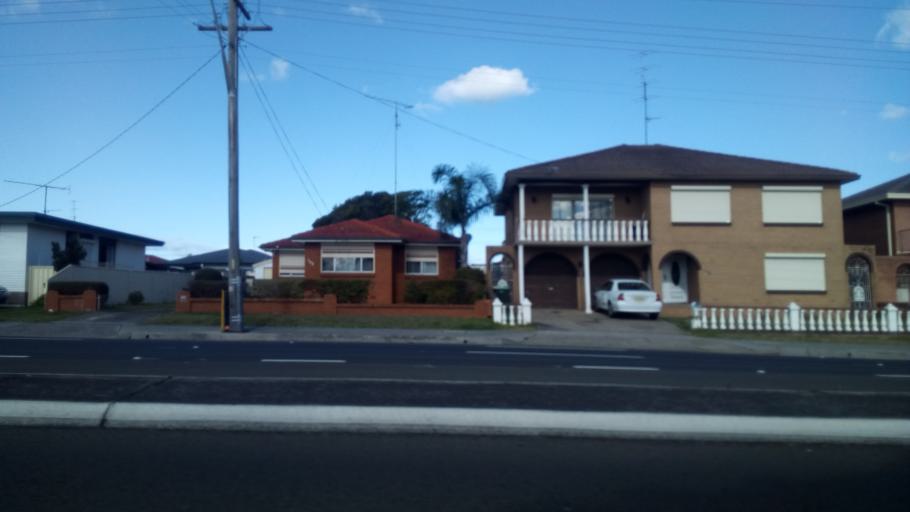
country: AU
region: New South Wales
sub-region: Shellharbour
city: Lake Illawarra
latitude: -34.5558
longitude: 150.8483
